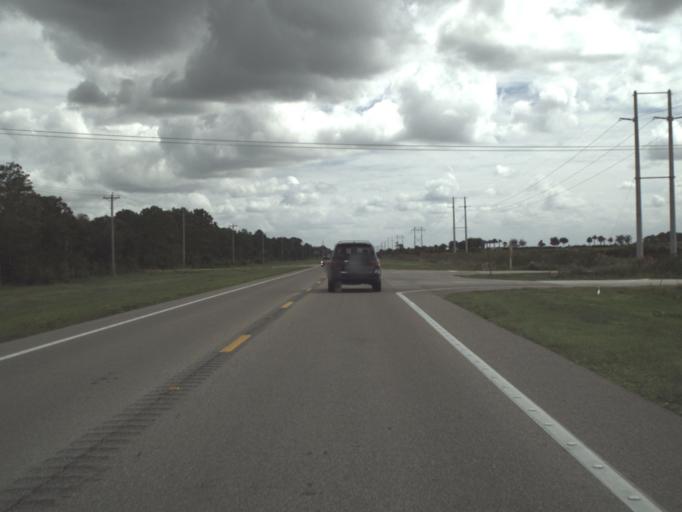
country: US
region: Florida
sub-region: Lee County
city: Lehigh Acres
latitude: 26.5320
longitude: -81.6170
